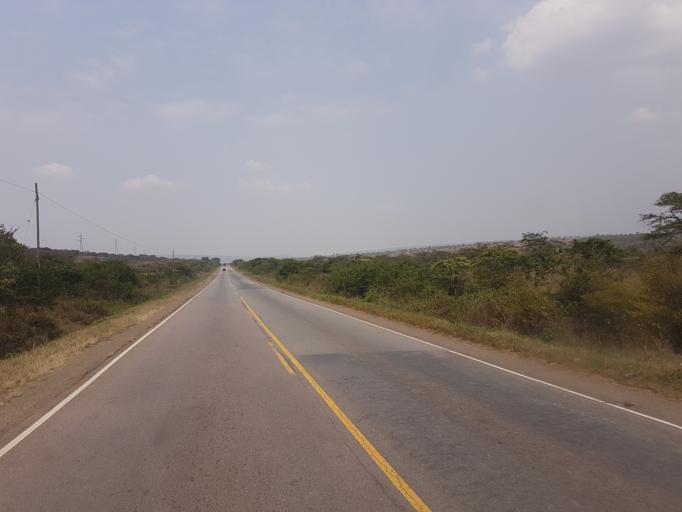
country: UG
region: Western Region
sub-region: Mbarara District
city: Mbarara
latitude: -0.5105
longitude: 30.7920
